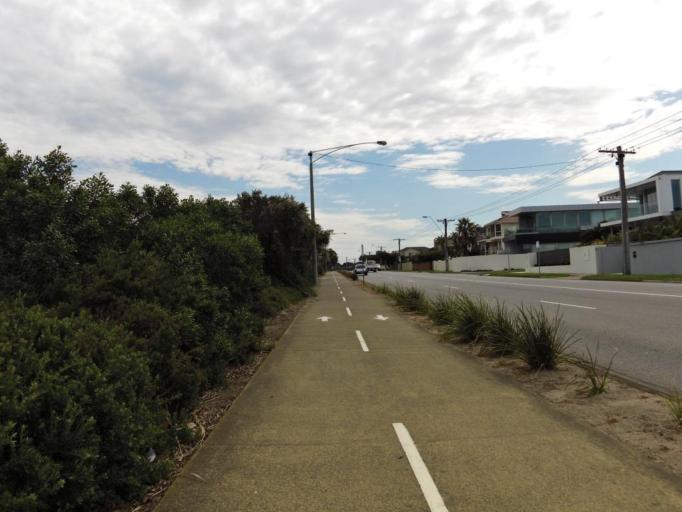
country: AU
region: Victoria
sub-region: Bayside
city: Black Rock
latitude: -37.9735
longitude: 145.0143
